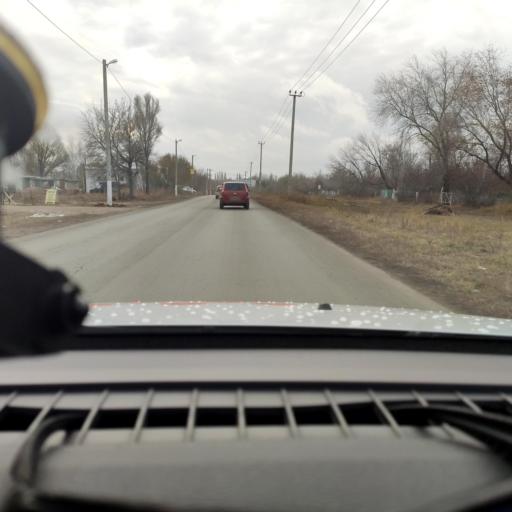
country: RU
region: Samara
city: Chapayevsk
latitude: 52.9905
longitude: 49.7282
